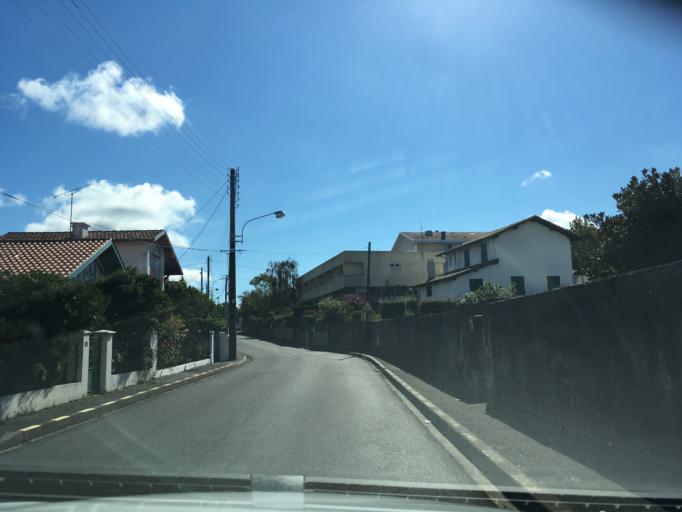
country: FR
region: Aquitaine
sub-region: Departement des Pyrenees-Atlantiques
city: Boucau
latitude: 43.5055
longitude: -1.4728
